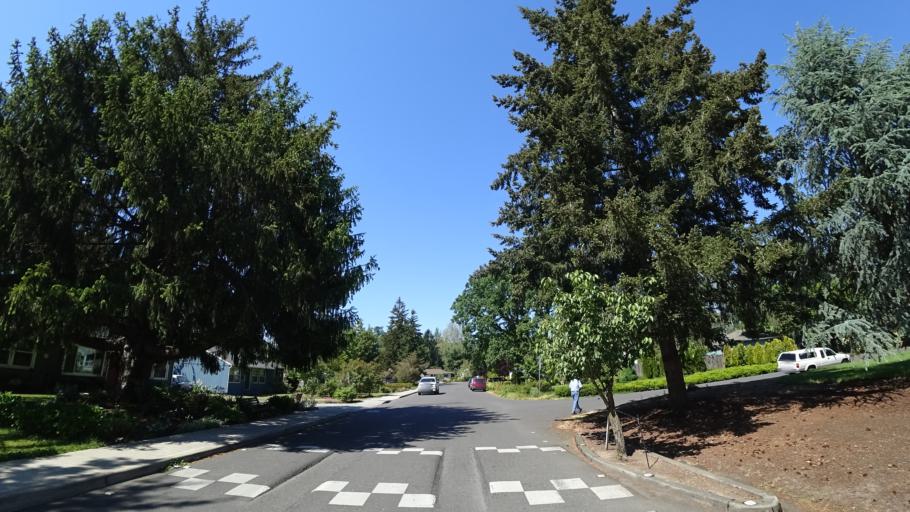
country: US
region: Oregon
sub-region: Washington County
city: Beaverton
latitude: 45.4961
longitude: -122.8045
